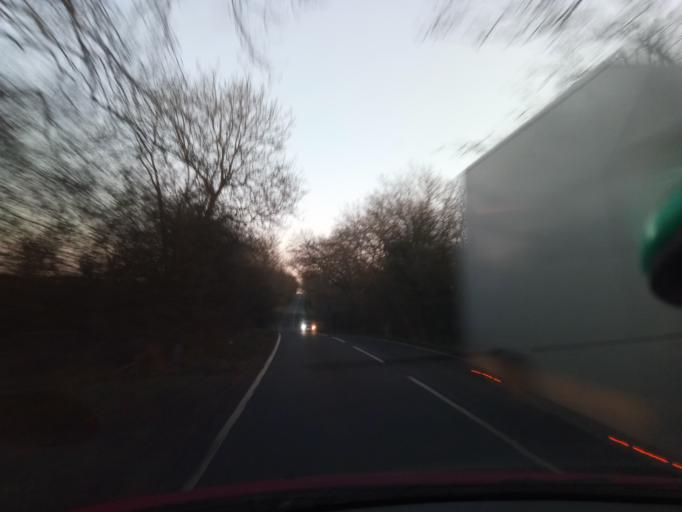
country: GB
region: England
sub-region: Leicestershire
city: Sileby
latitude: 52.7574
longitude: -1.0990
